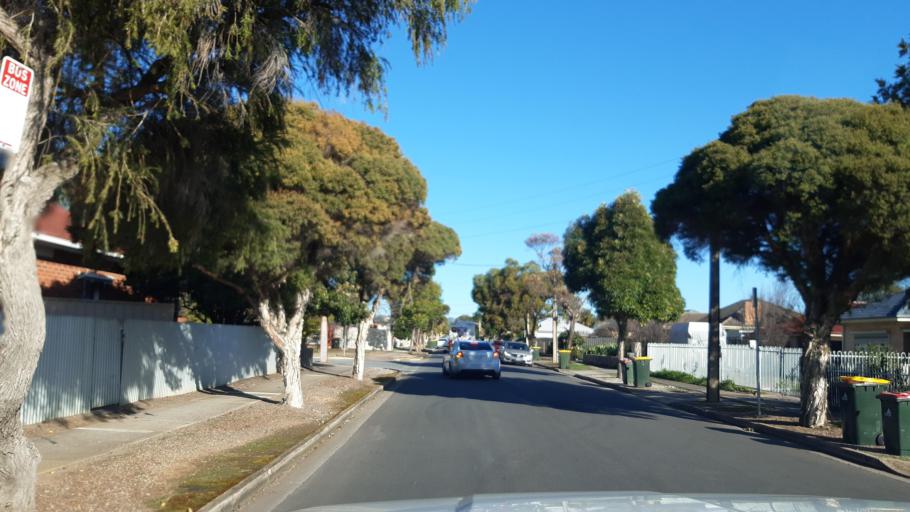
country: AU
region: South Australia
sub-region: Marion
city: Clovelly Park
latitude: -34.9938
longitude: 138.5670
